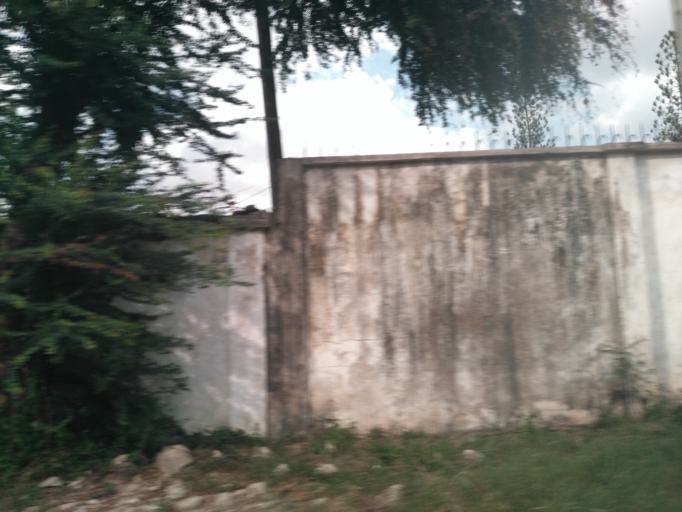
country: TZ
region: Dar es Salaam
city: Magomeni
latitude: -6.7419
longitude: 39.2397
